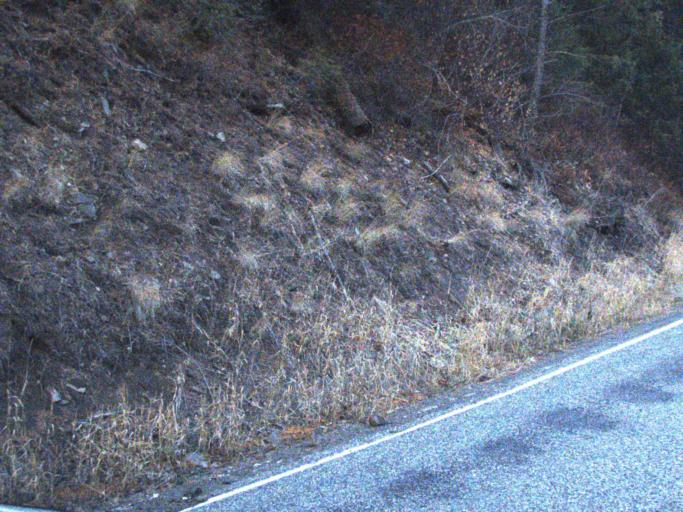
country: US
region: Washington
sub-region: Ferry County
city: Republic
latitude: 48.5549
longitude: -118.7438
